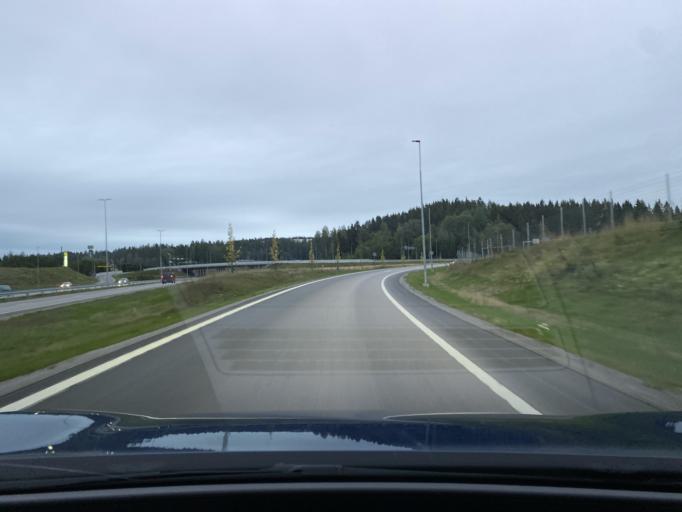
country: FI
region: Paijanne Tavastia
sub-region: Lahti
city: Lahti
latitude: 60.9558
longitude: 25.6463
